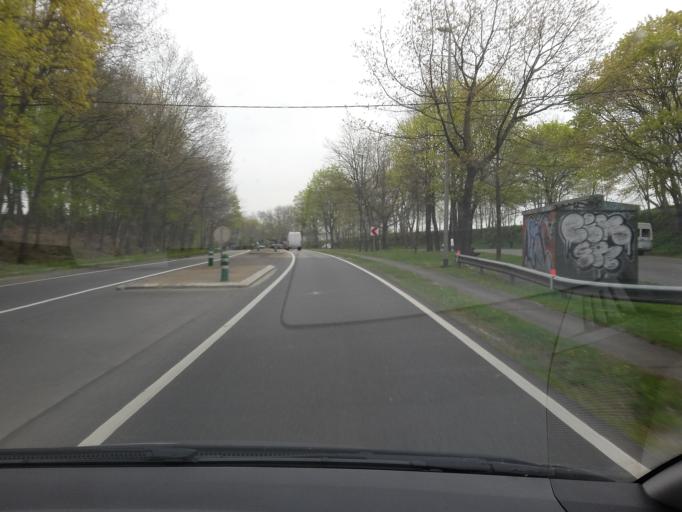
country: BE
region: Wallonia
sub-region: Province du Brabant Wallon
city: Braine-l'Alleud
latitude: 50.6554
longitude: 4.4129
